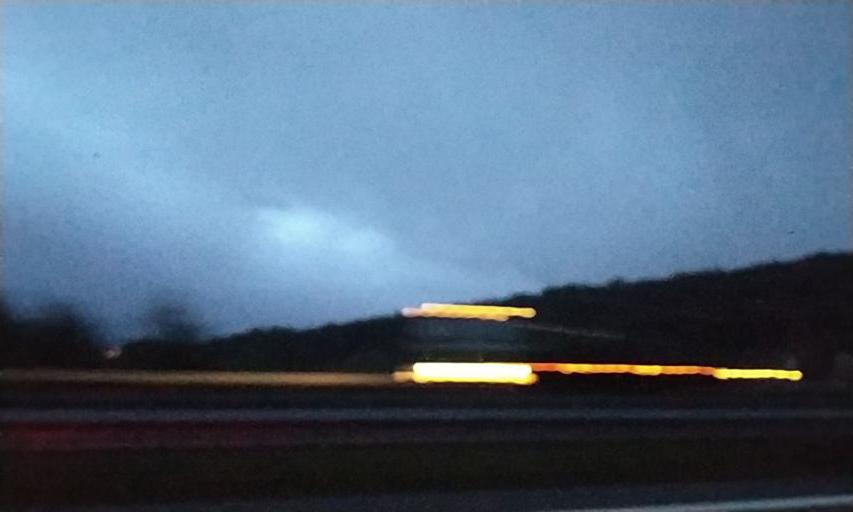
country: PT
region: Braga
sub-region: Guimaraes
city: Ronfe
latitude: 41.4811
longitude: -8.3977
